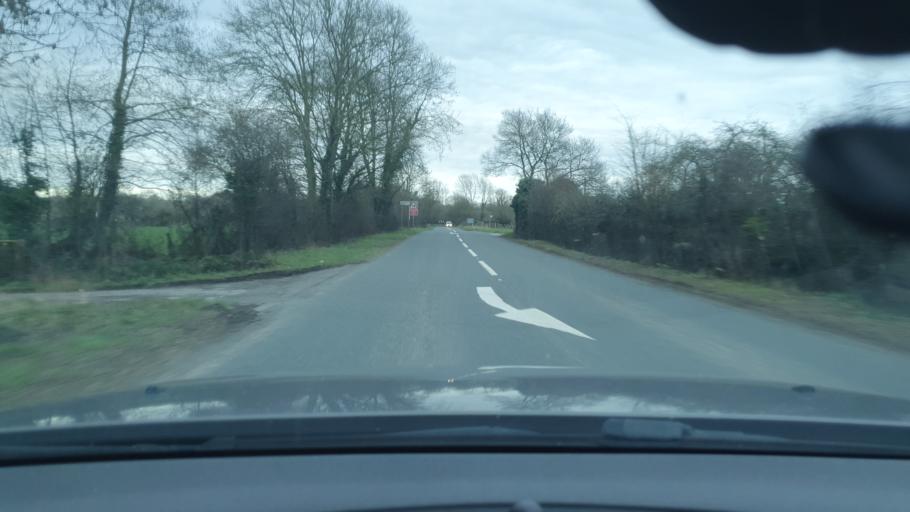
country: GB
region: England
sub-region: Wiltshire
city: Seend
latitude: 51.3362
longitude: -2.1130
